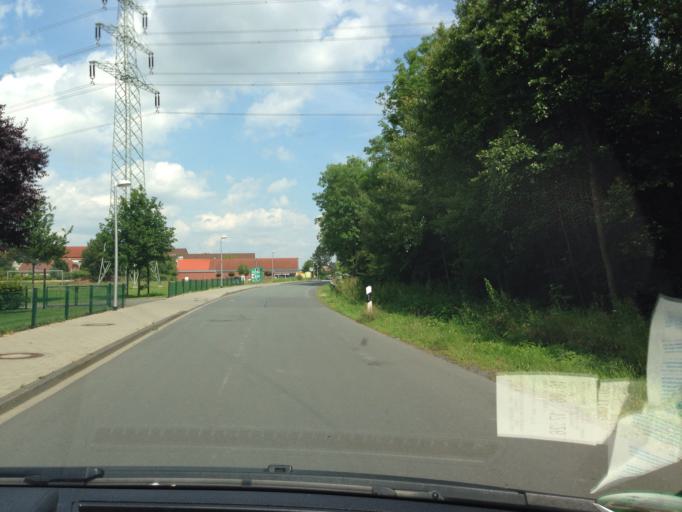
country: DE
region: North Rhine-Westphalia
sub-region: Regierungsbezirk Munster
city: Muenster
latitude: 51.9933
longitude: 7.5450
